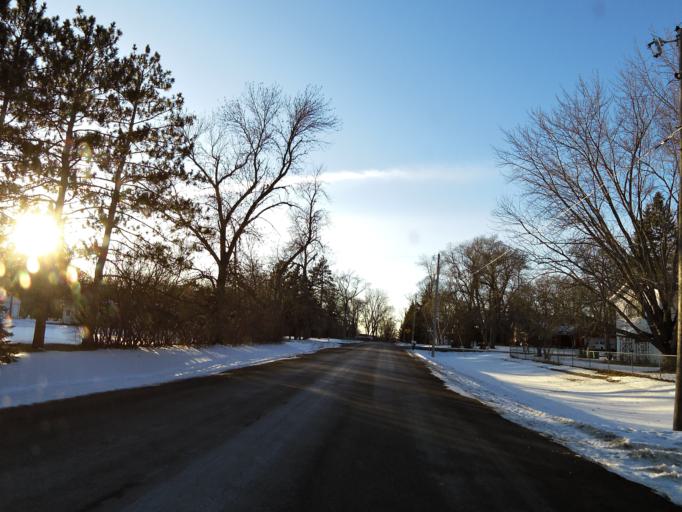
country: US
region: Minnesota
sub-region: Washington County
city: Cottage Grove
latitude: 44.8371
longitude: -92.8800
